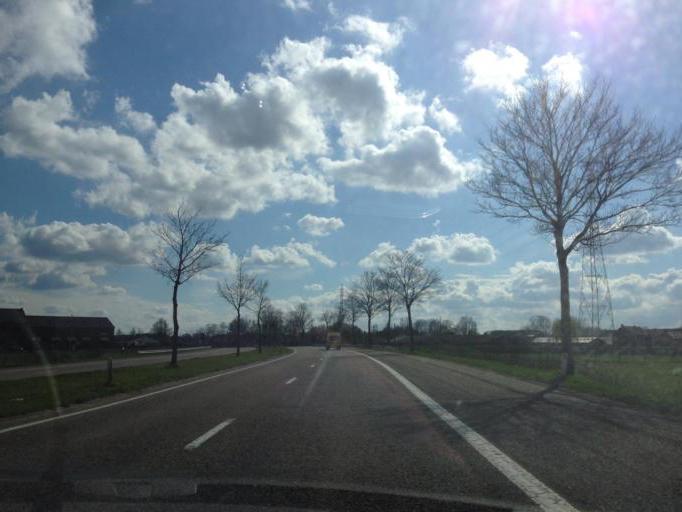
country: BE
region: Flanders
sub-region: Provincie Limburg
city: Bree
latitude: 51.1503
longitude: 5.5856
